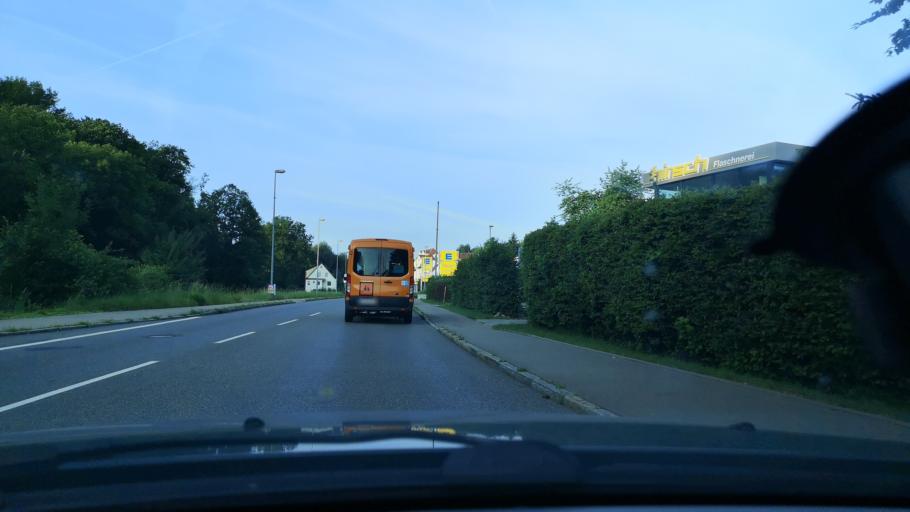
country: DE
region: Baden-Wuerttemberg
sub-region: Regierungsbezirk Stuttgart
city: Albershausen
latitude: 48.6991
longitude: 9.5708
